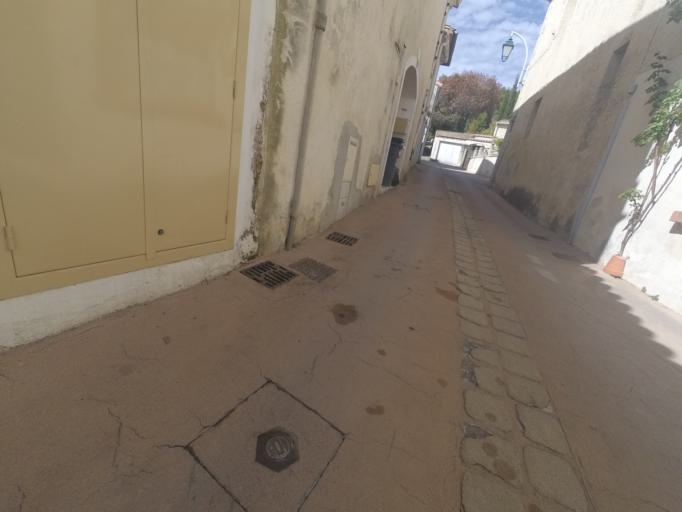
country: FR
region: Languedoc-Roussillon
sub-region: Departement du Gard
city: Nages-et-Solorgues
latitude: 43.7916
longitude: 4.2293
